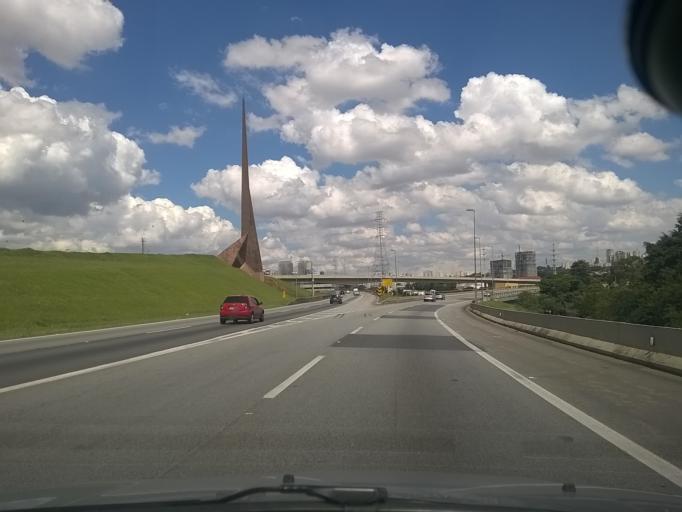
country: BR
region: Sao Paulo
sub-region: Osasco
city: Osasco
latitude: -23.5076
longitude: -46.7217
